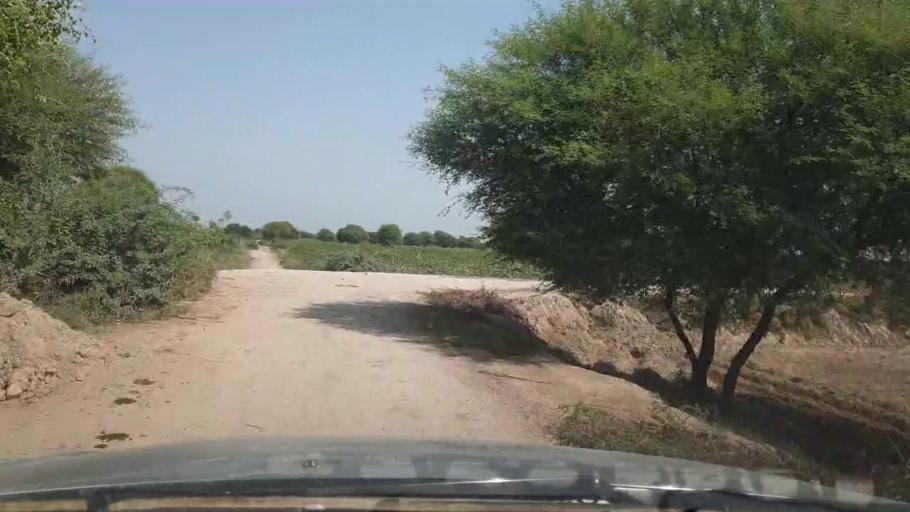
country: PK
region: Sindh
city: Tando Ghulam Ali
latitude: 25.1588
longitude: 68.8946
